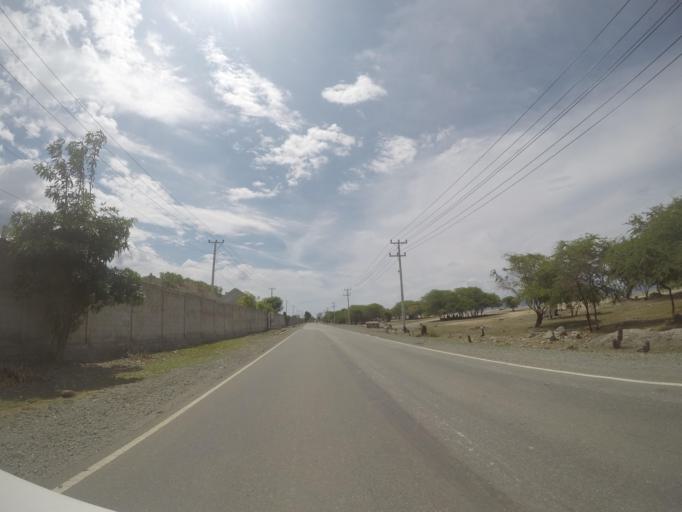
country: TL
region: Liquica
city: Liquica
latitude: -8.5644
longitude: 125.4066
